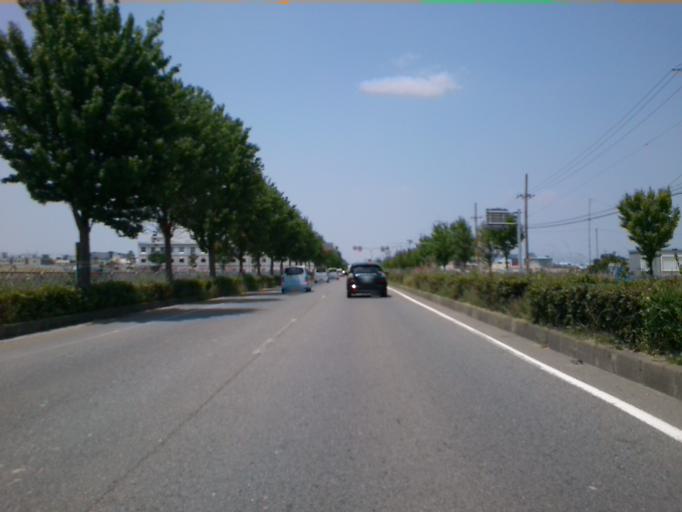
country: JP
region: Kyoto
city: Tanabe
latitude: 34.8587
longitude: 135.7622
